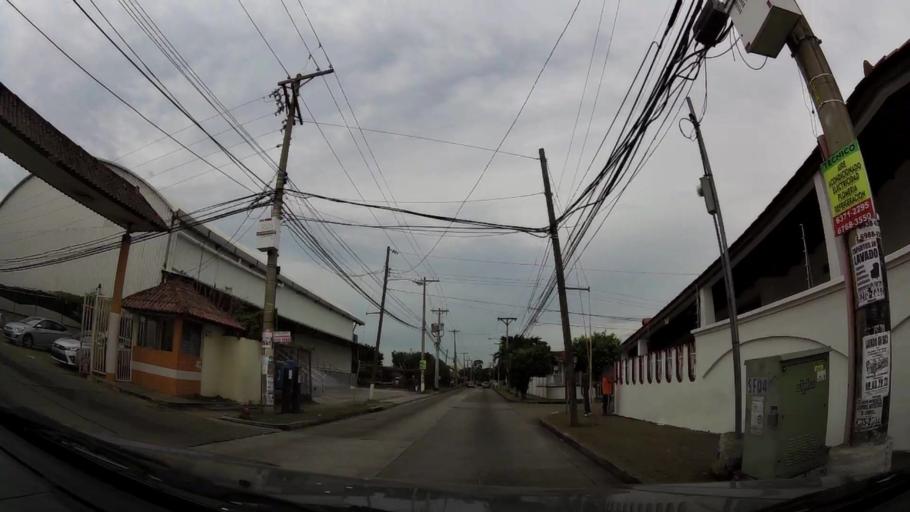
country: PA
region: Panama
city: San Miguelito
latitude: 9.0287
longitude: -79.4713
